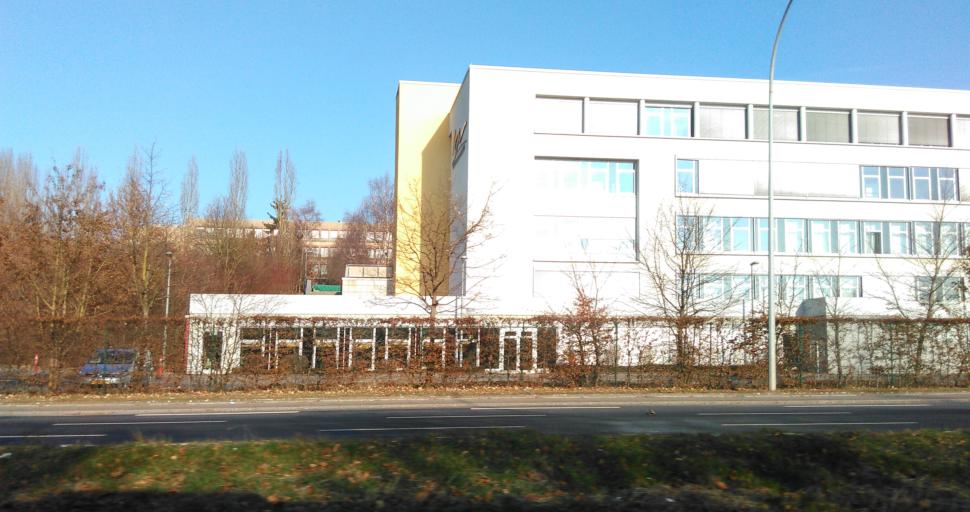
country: LU
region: Luxembourg
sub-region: Canton de Luxembourg
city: Luxembourg
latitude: 49.6000
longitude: 6.1106
